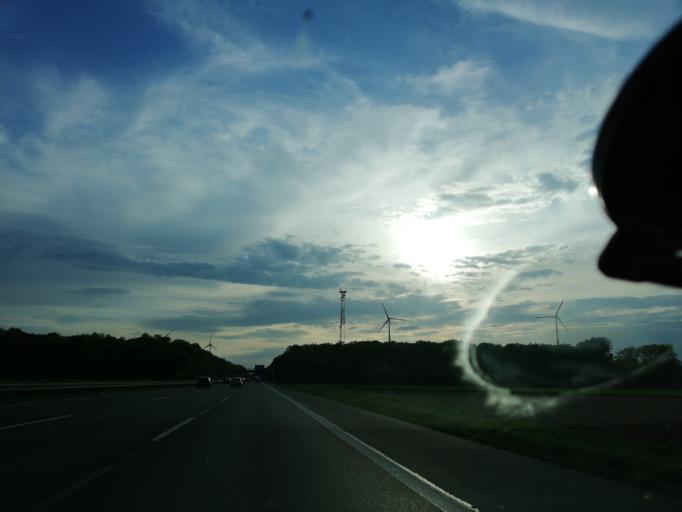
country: DE
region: North Rhine-Westphalia
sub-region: Regierungsbezirk Detmold
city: Rheda-Wiedenbruck
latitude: 51.8321
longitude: 8.2404
